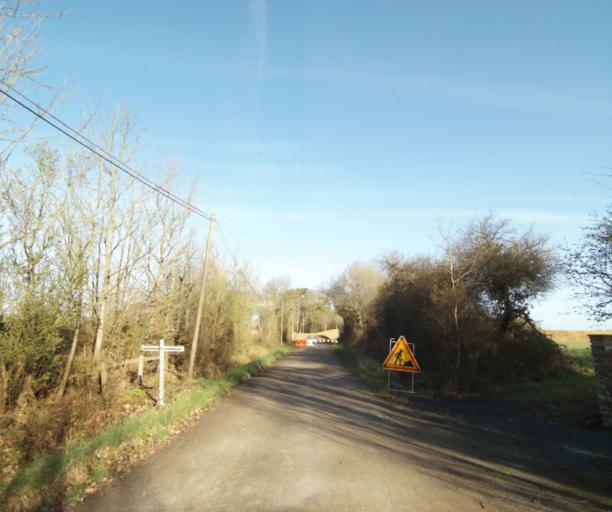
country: FR
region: Pays de la Loire
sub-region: Departement de la Loire-Atlantique
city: Bouvron
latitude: 47.4134
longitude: -1.8348
